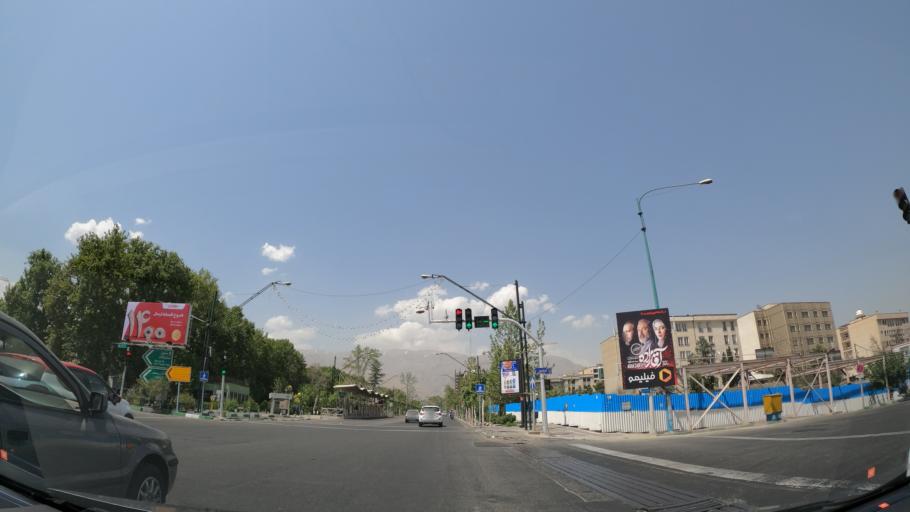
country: IR
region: Tehran
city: Tajrish
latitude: 35.7715
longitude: 51.4121
